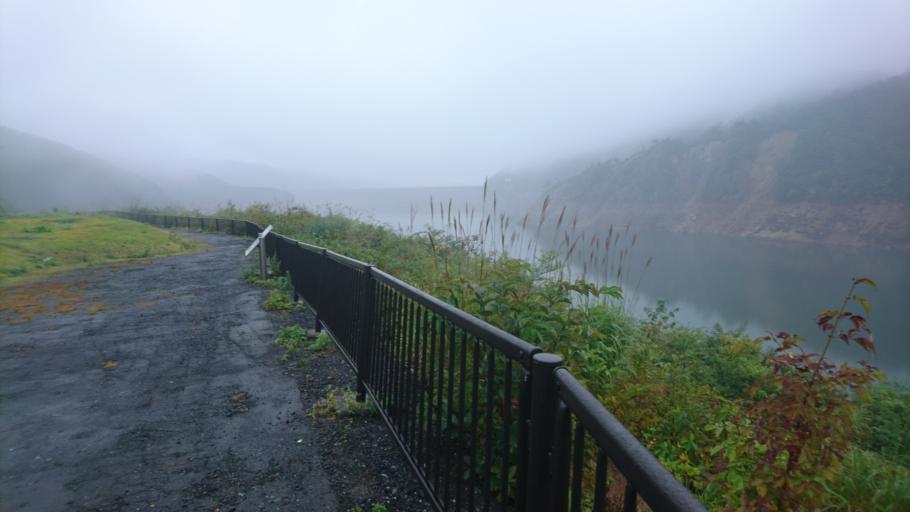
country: JP
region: Iwate
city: Mizusawa
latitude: 39.1155
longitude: 140.9028
